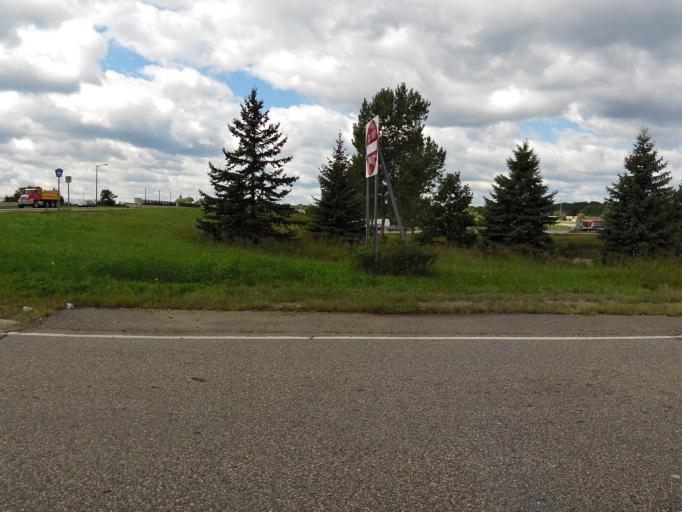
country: US
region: Minnesota
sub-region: Dakota County
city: Burnsville
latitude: 44.7144
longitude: -93.2814
